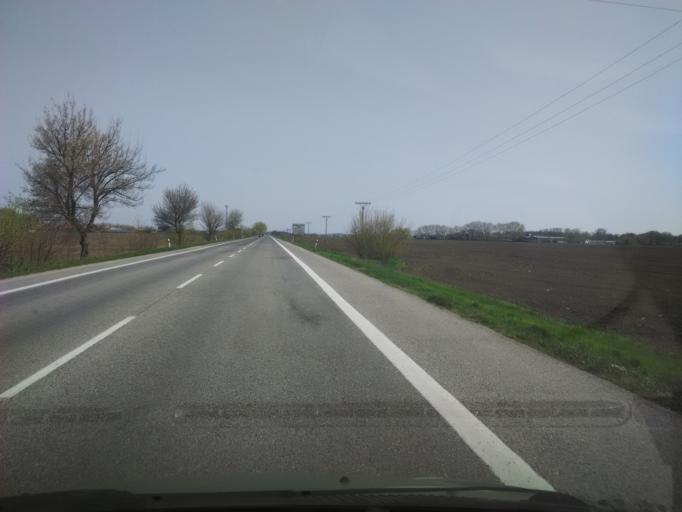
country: SK
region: Trnavsky
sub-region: Okres Galanta
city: Galanta
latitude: 48.1811
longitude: 17.7805
